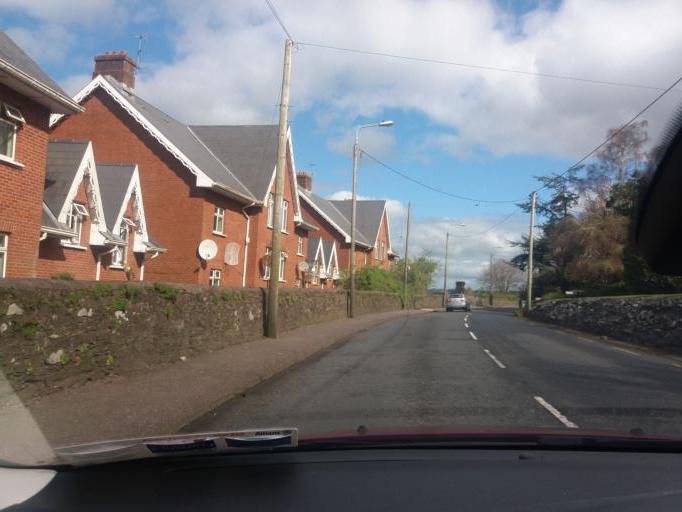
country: IE
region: Munster
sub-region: County Cork
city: Passage West
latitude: 51.8541
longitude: -8.3272
